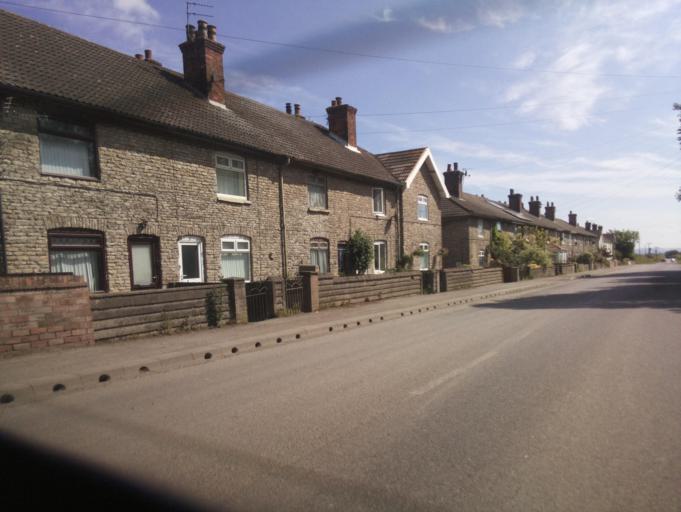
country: GB
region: England
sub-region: North Lincolnshire
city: Redbourne
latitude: 53.5008
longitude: -0.5670
